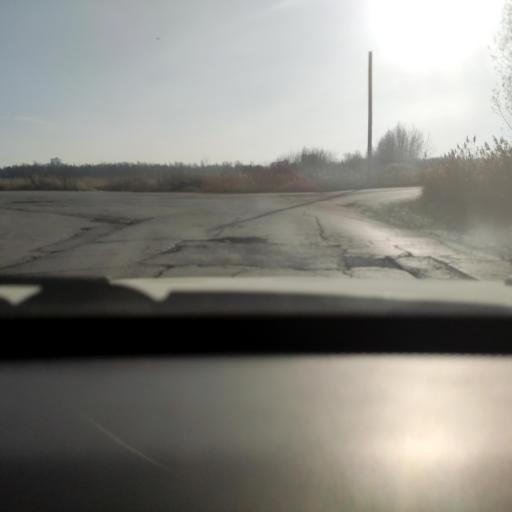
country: RU
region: Perm
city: Perm
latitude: 58.0350
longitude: 56.1912
